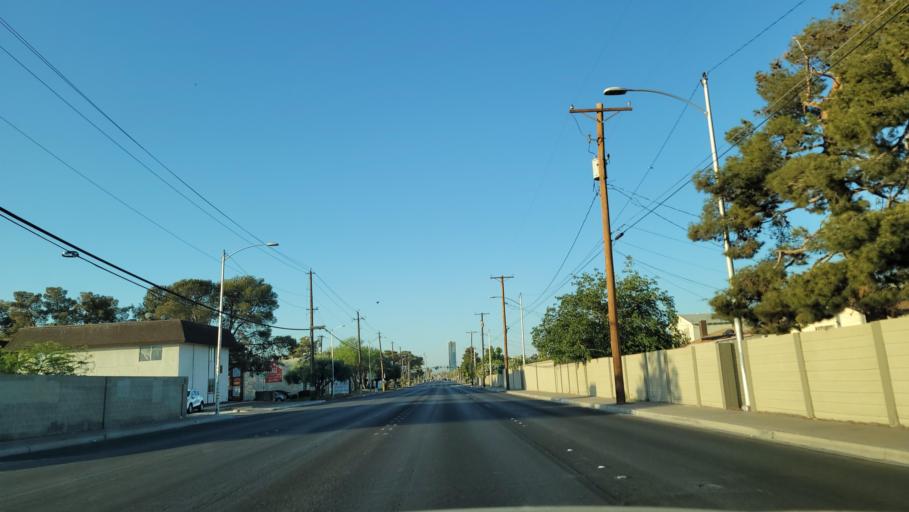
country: US
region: Nevada
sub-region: Clark County
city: Spring Valley
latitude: 36.1400
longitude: -115.1996
